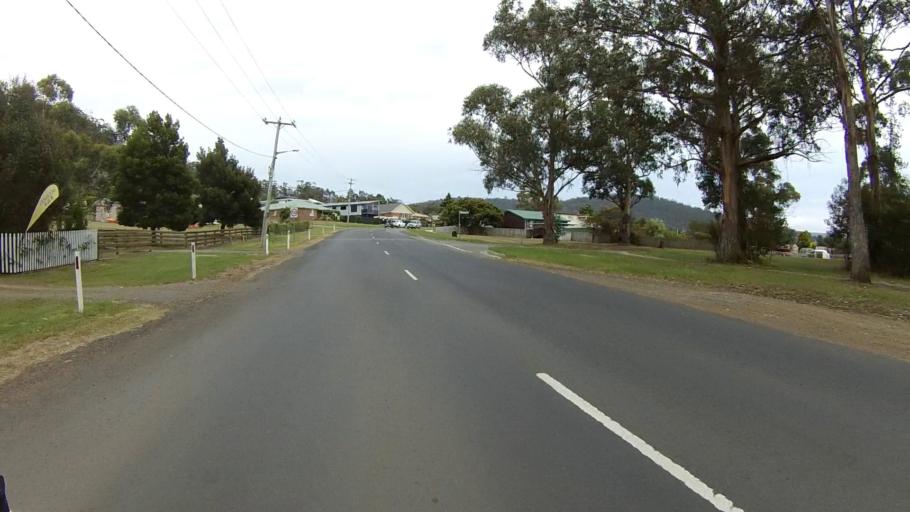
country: AU
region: Tasmania
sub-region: Sorell
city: Sorell
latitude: -42.5674
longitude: 147.8748
